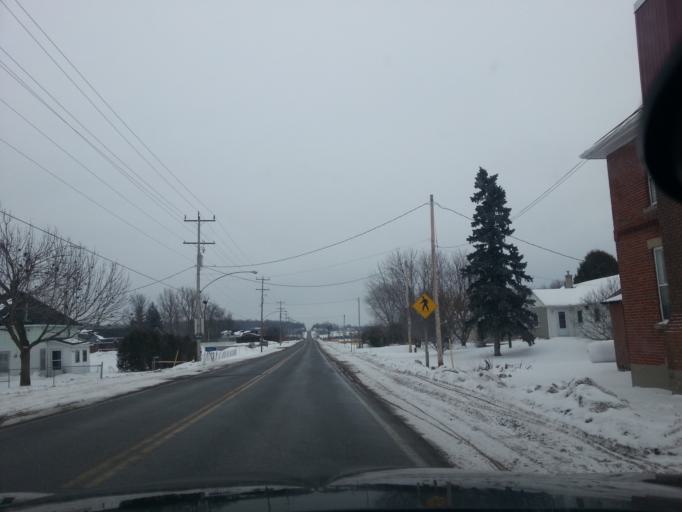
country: CA
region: Ontario
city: Arnprior
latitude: 45.3918
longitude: -76.1885
